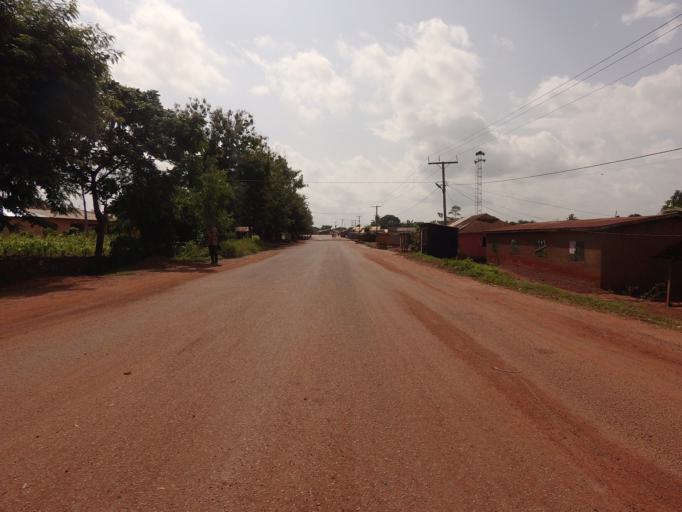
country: TG
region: Maritime
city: Tsevie
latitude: 6.3593
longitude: 0.8662
